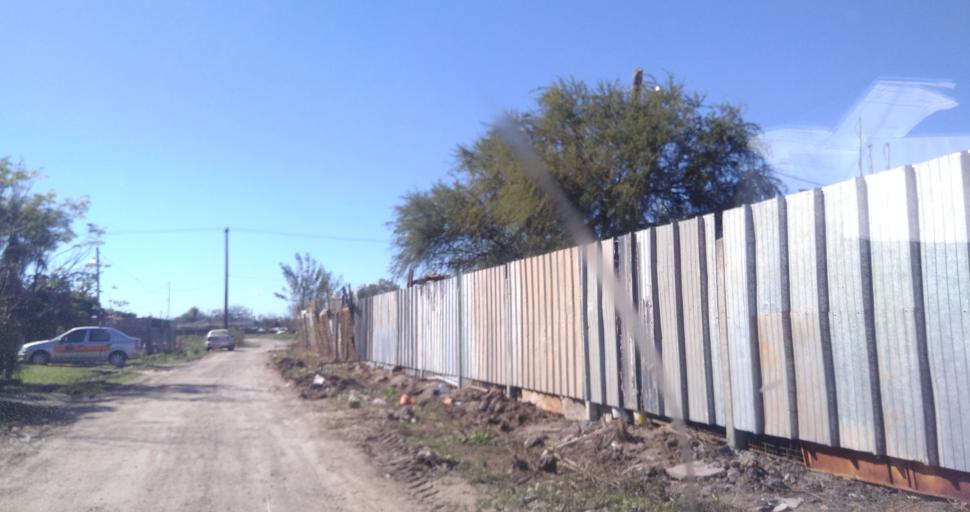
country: AR
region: Chaco
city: Fontana
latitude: -27.4311
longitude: -59.0211
